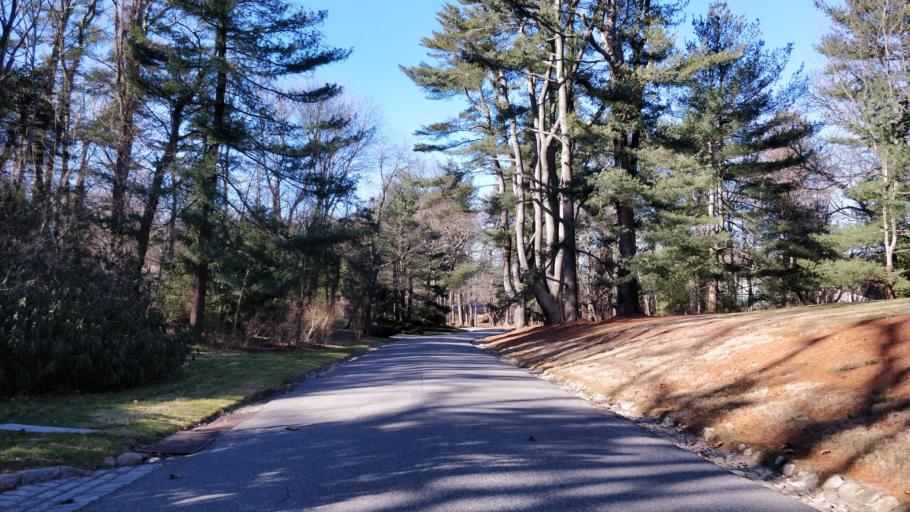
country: US
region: New York
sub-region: Nassau County
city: Brookville
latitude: 40.8207
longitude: -73.5664
